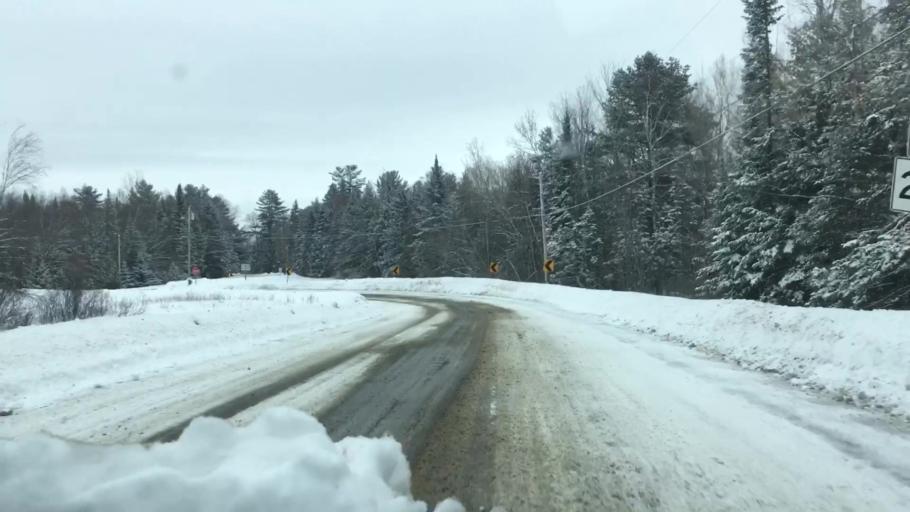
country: US
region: Maine
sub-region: Penobscot County
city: Hudson
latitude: 45.0215
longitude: -68.9156
